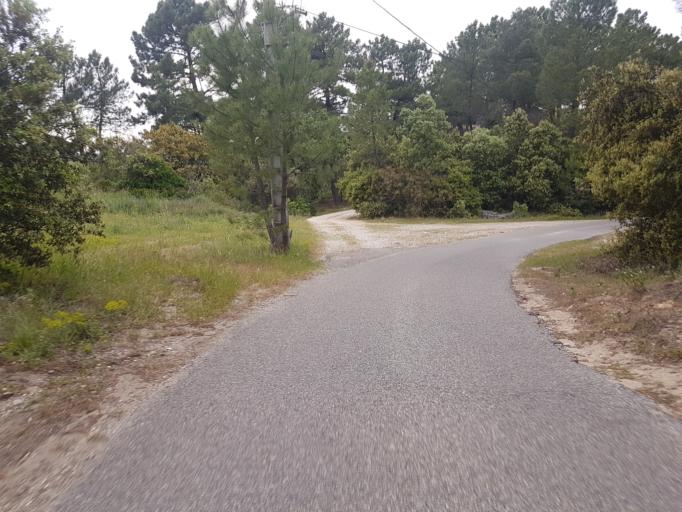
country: FR
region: Provence-Alpes-Cote d'Azur
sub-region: Departement du Vaucluse
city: Mondragon
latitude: 44.2424
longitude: 4.7243
